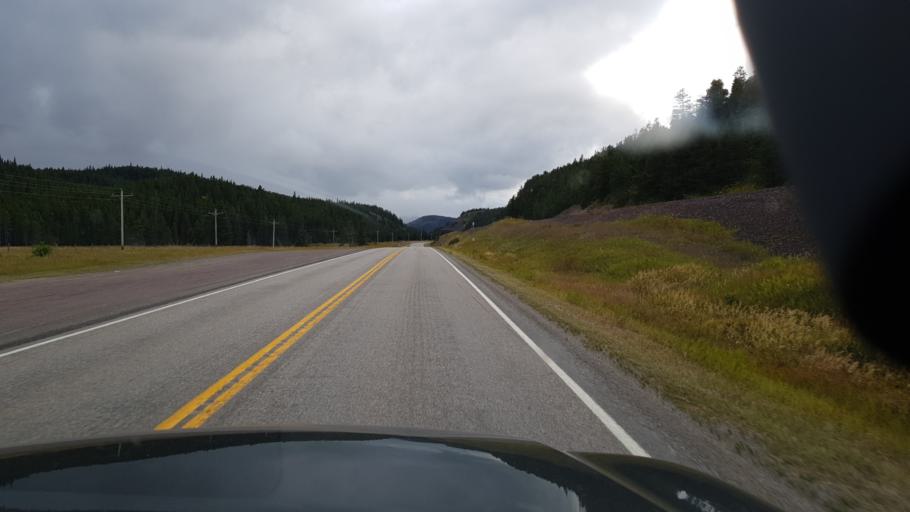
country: US
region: Montana
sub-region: Glacier County
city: South Browning
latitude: 48.3370
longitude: -113.3283
